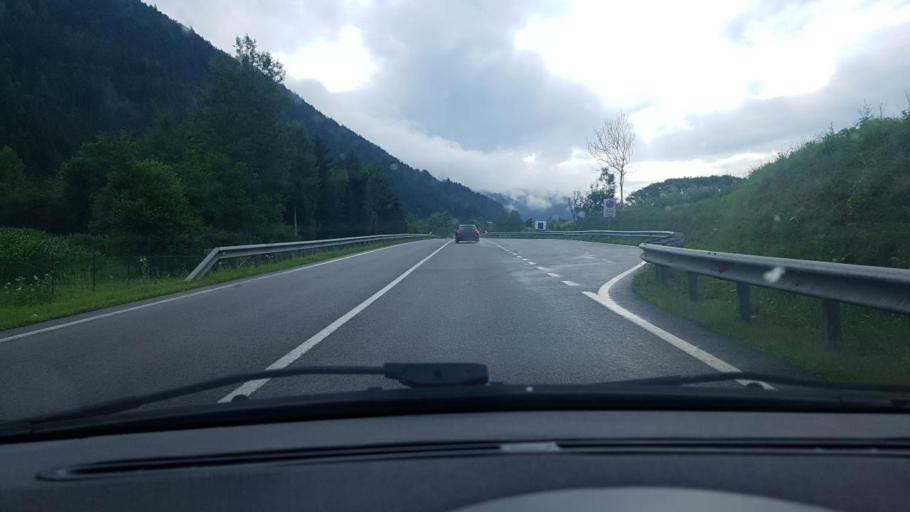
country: IT
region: Trentino-Alto Adige
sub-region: Bolzano
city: Terento
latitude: 46.8099
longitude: 11.7720
